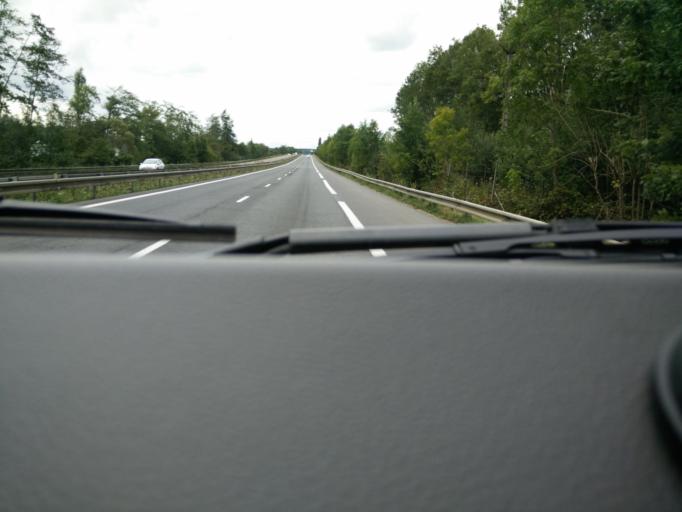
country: FR
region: Champagne-Ardenne
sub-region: Departement des Ardennes
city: Vrigne-aux-Bois
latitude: 49.7244
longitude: 4.8460
